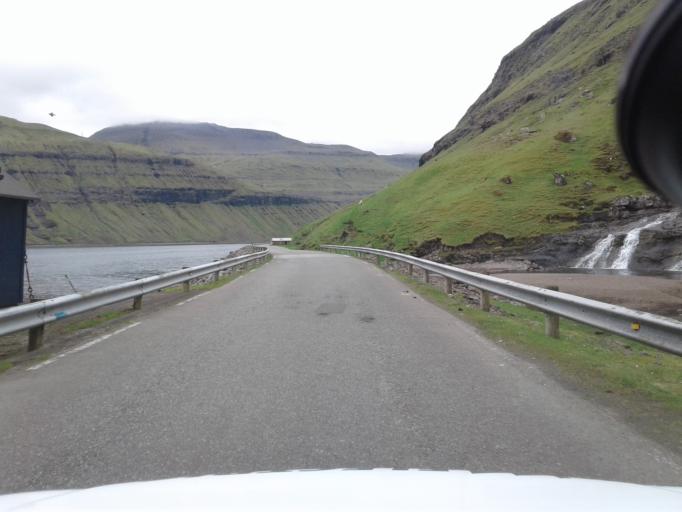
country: FO
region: Streymoy
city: Kollafjordhur
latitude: 62.0613
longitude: -6.8762
